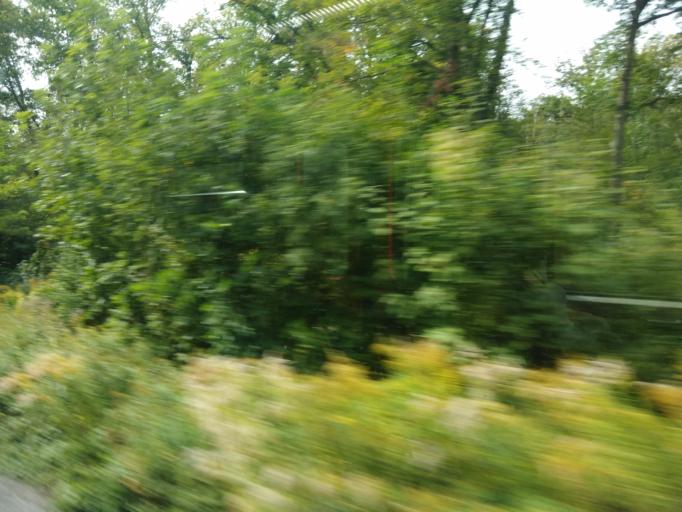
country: DE
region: Baden-Wuerttemberg
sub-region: Karlsruhe Region
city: Weingarten
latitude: 49.0762
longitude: 8.5373
